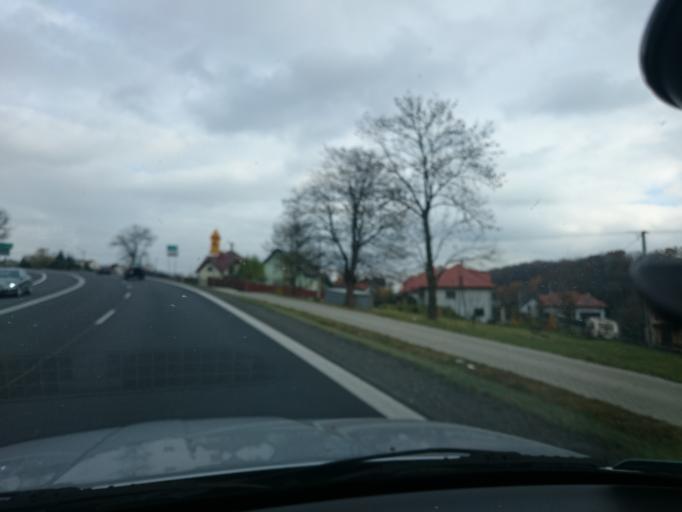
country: PL
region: Lesser Poland Voivodeship
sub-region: Powiat krakowski
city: Michalowice
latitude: 50.1746
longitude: 19.9865
